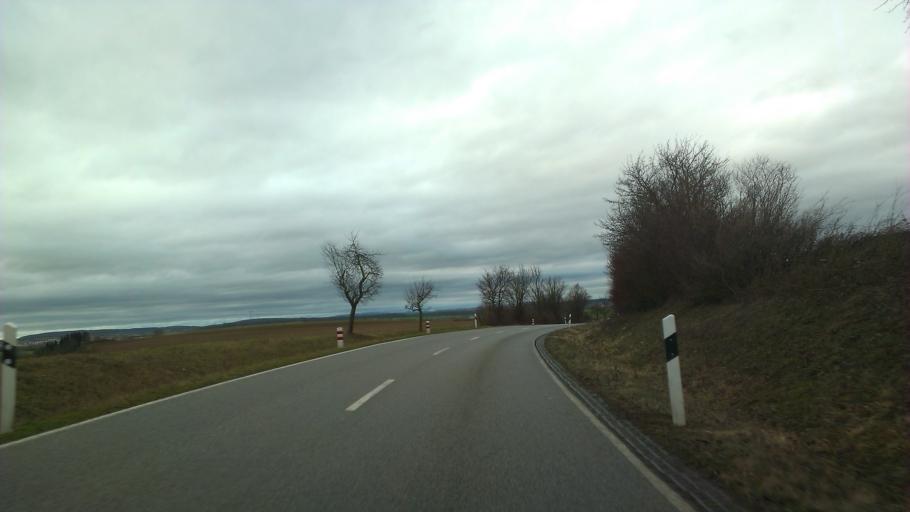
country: DE
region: Baden-Wuerttemberg
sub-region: Regierungsbezirk Stuttgart
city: Eppingen
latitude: 49.1084
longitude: 8.8996
